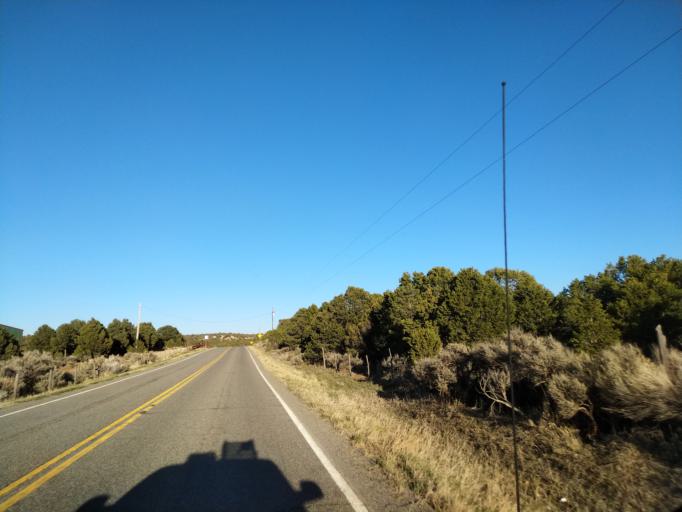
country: US
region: Colorado
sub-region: Mesa County
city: Redlands
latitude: 38.9938
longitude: -108.7235
